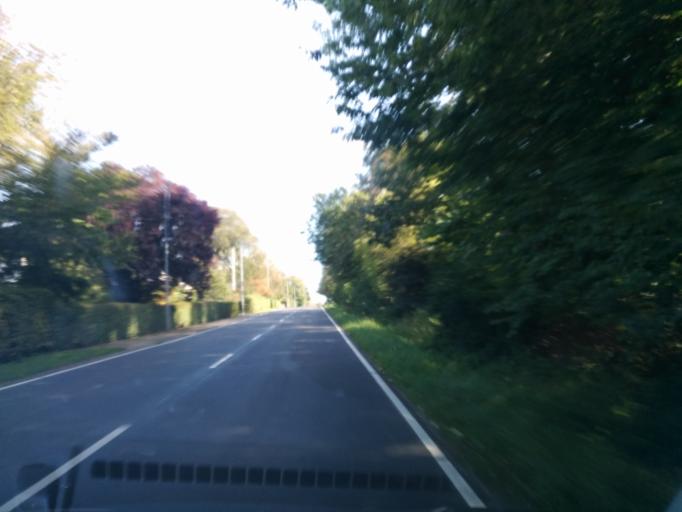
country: DK
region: South Denmark
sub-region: Kolding Kommune
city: Sonder Bjert
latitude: 55.4051
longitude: 9.5332
